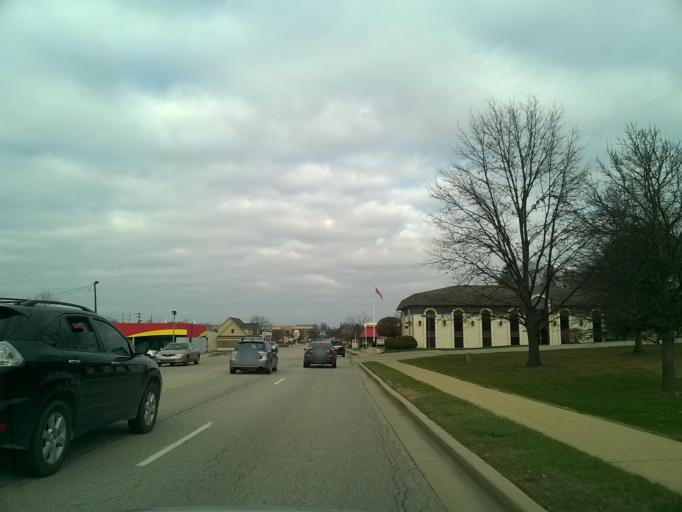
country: US
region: Indiana
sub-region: Hamilton County
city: Carmel
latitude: 39.9726
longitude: -86.1270
